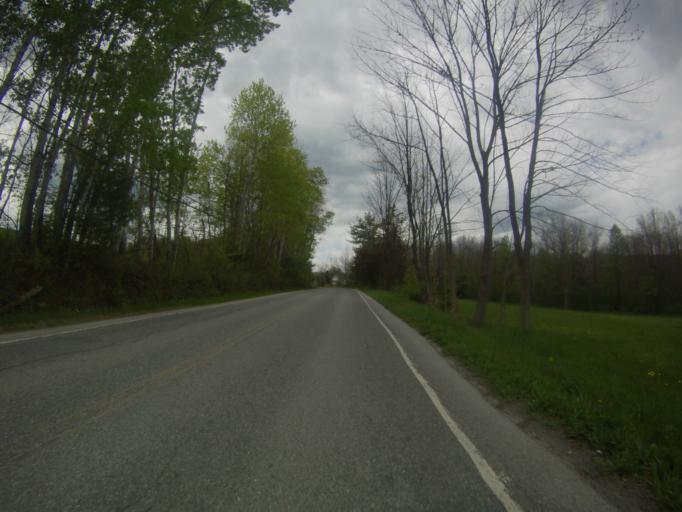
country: US
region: New York
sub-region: Essex County
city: Port Henry
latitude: 43.9503
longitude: -73.4764
